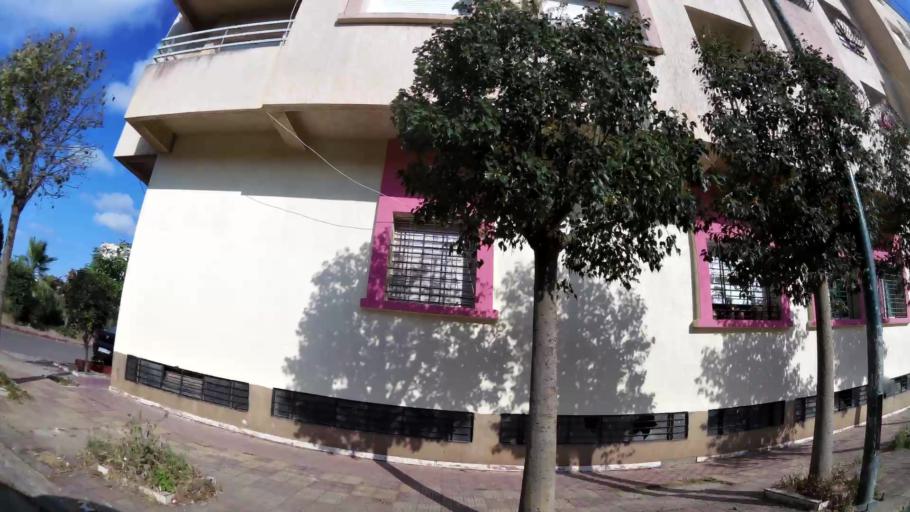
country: MA
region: Rabat-Sale-Zemmour-Zaer
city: Sale
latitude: 34.0520
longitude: -6.8002
